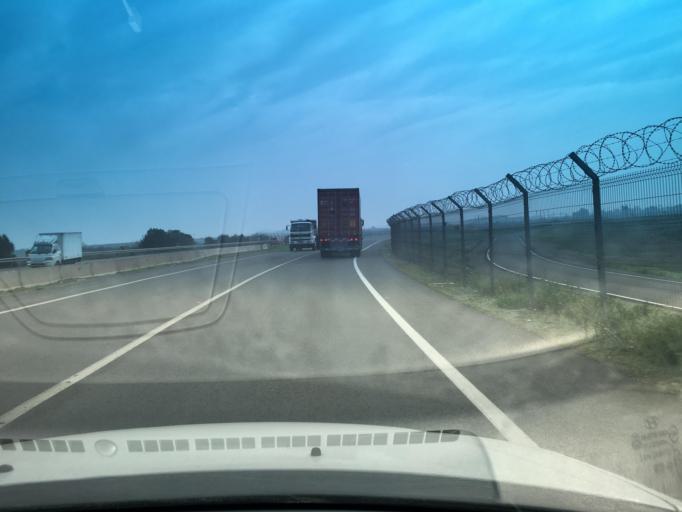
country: CL
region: Santiago Metropolitan
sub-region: Provincia de Chacabuco
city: Lampa
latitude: -33.3683
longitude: -70.8051
